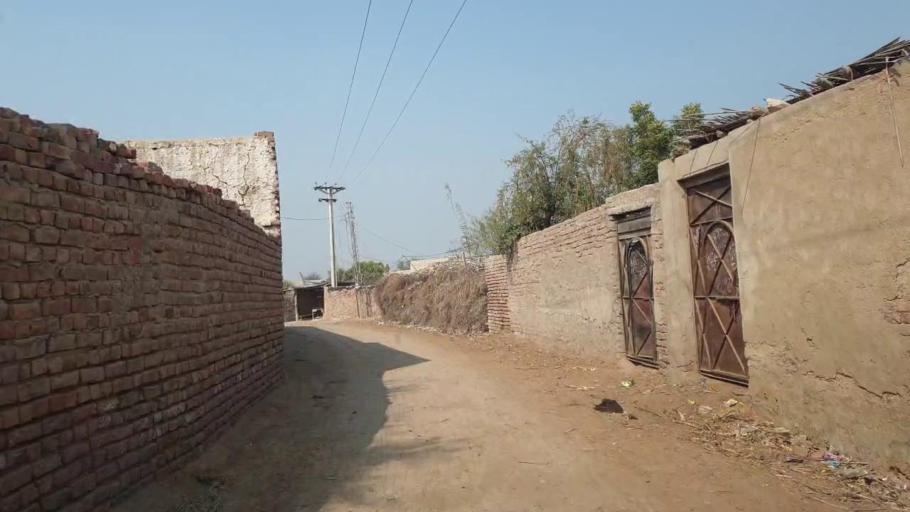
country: PK
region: Sindh
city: Hala
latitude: 25.9495
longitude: 68.4683
